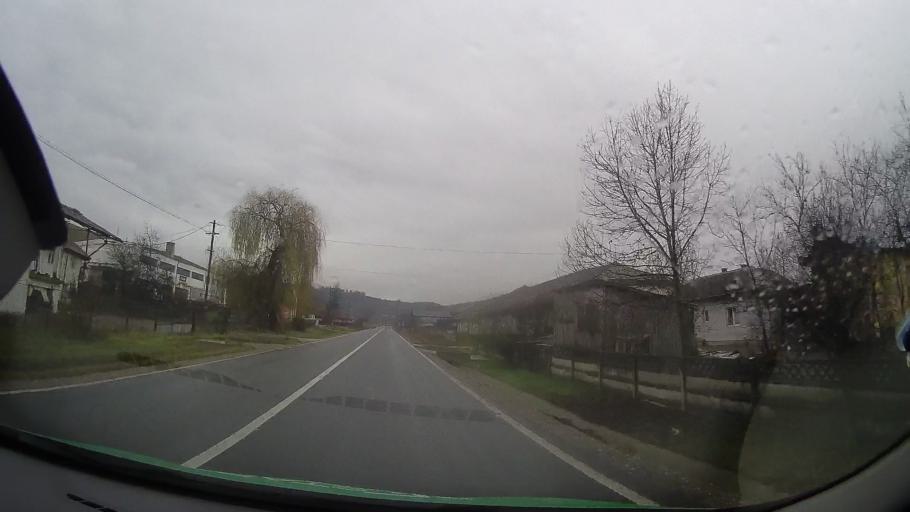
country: RO
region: Bistrita-Nasaud
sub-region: Comuna Teaca
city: Teaca
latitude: 46.9171
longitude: 24.4945
